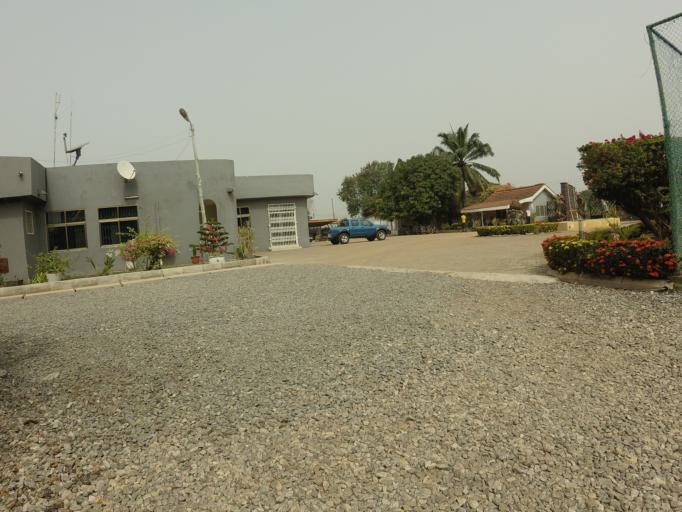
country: GH
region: Volta
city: Anloga
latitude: 5.9912
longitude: 0.5939
